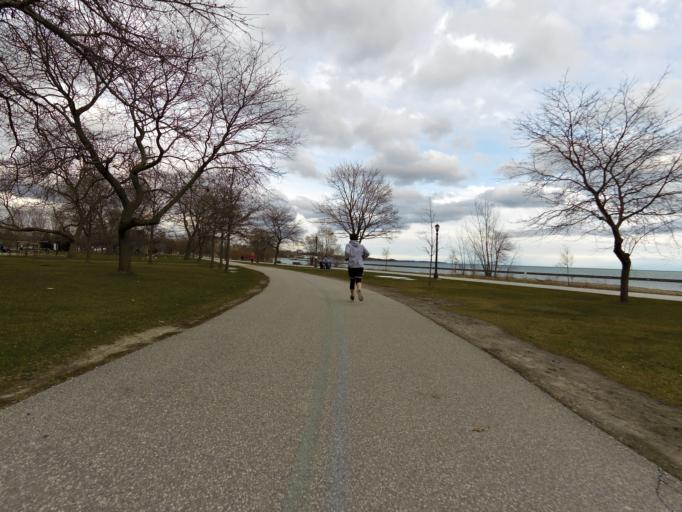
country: CA
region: Ontario
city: Toronto
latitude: 43.6363
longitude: -79.4634
